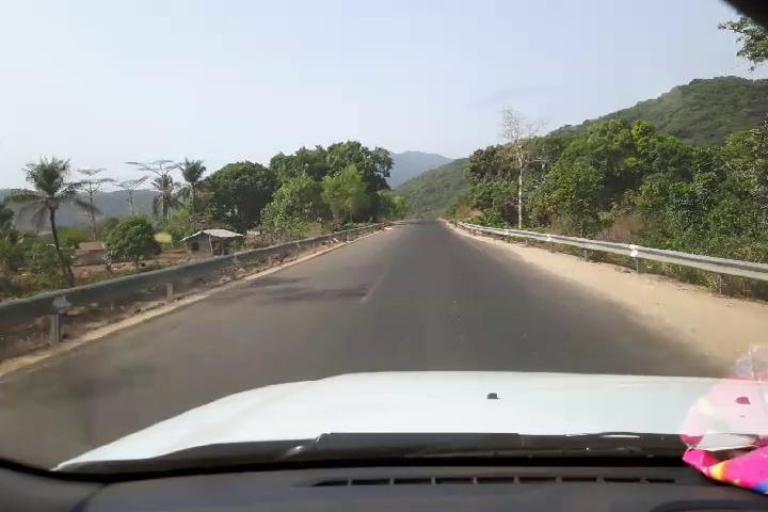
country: SL
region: Western Area
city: Hastings
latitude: 8.2744
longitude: -13.1572
